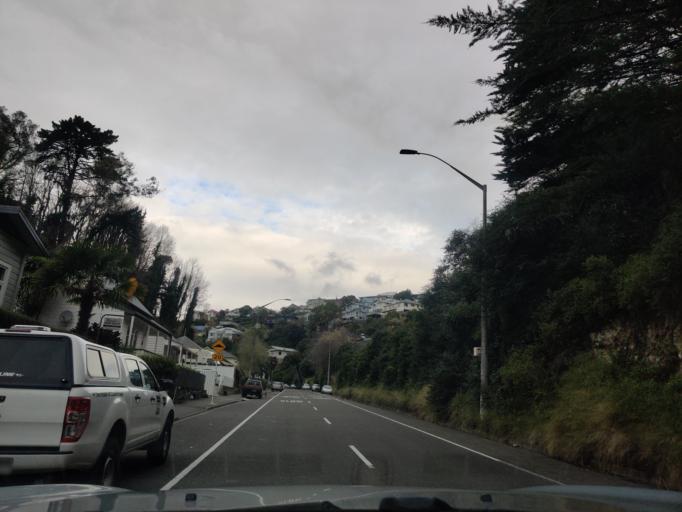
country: NZ
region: Hawke's Bay
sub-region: Napier City
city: Napier
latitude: -39.4827
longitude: 176.9097
